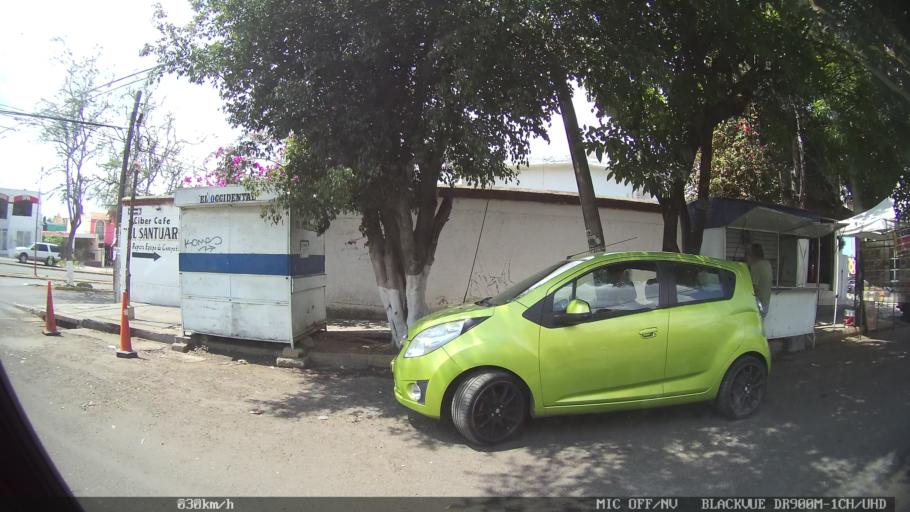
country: MX
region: Jalisco
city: Tonala
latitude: 20.6246
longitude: -103.2559
